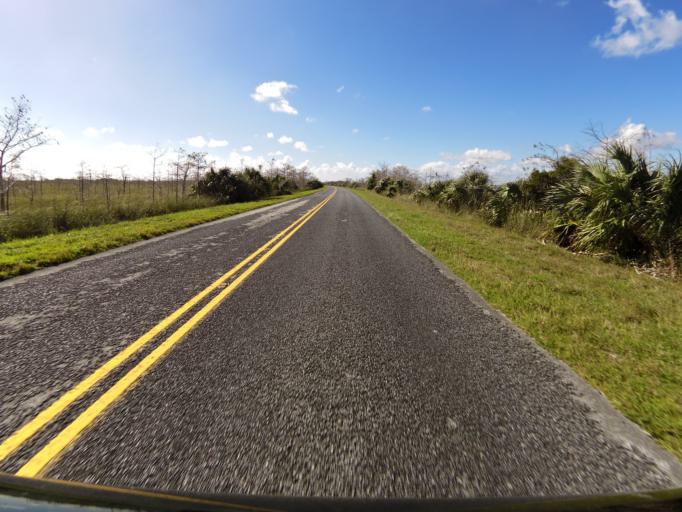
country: US
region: Florida
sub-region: Miami-Dade County
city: Florida City
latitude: 25.4315
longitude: -80.7643
